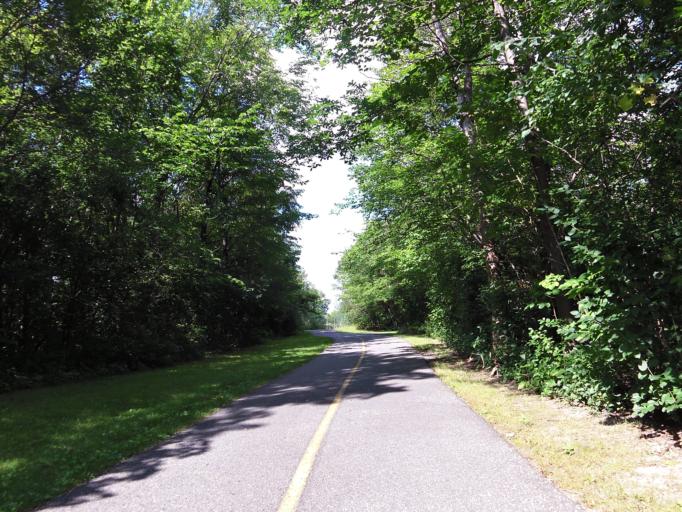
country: CA
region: Ontario
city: Ottawa
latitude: 45.3698
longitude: -75.7442
